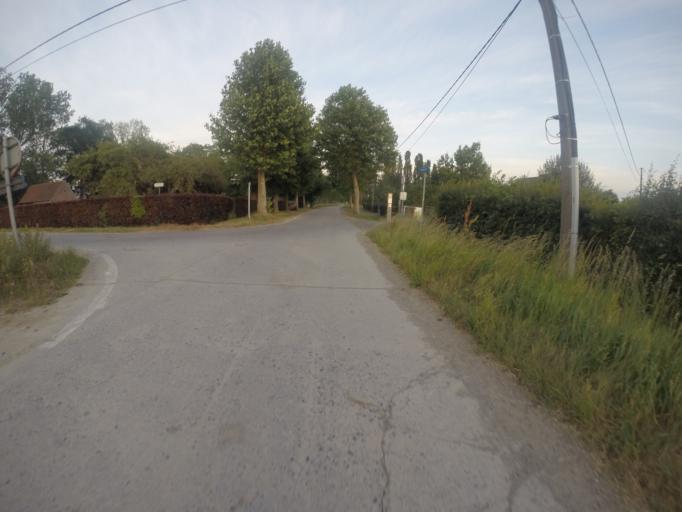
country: BE
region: Flanders
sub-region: Provincie Oost-Vlaanderen
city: Zomergem
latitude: 51.1264
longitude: 3.5249
